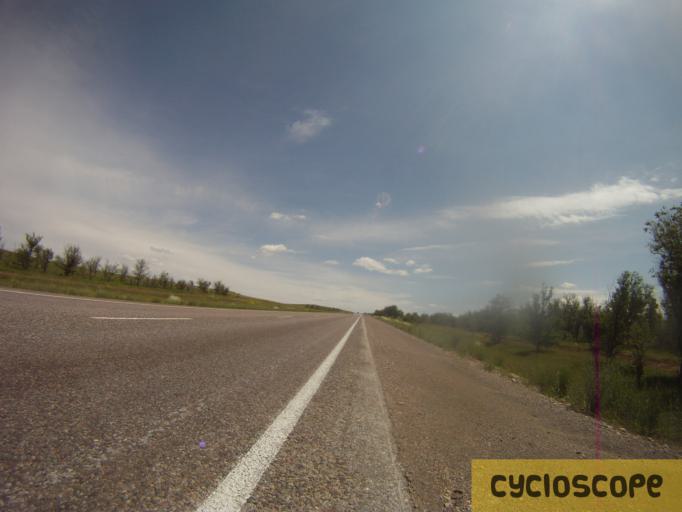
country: KZ
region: Zhambyl
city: Georgiyevka
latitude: 43.3014
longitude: 74.8935
